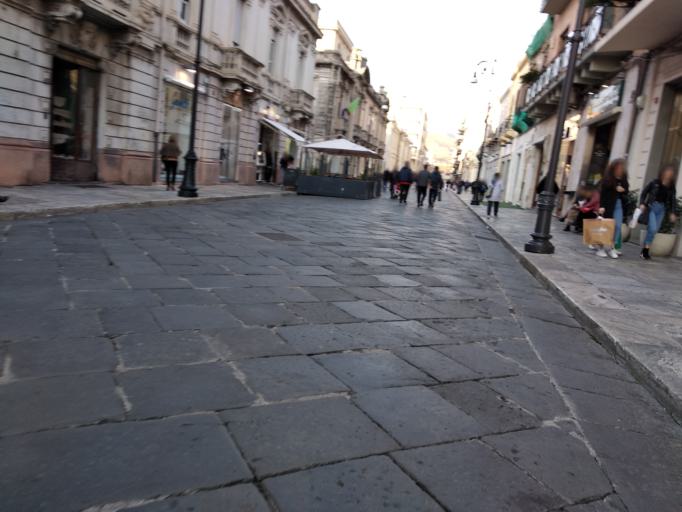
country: IT
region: Calabria
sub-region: Provincia di Reggio Calabria
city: Reggio Calabria
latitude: 38.1104
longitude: 15.6463
